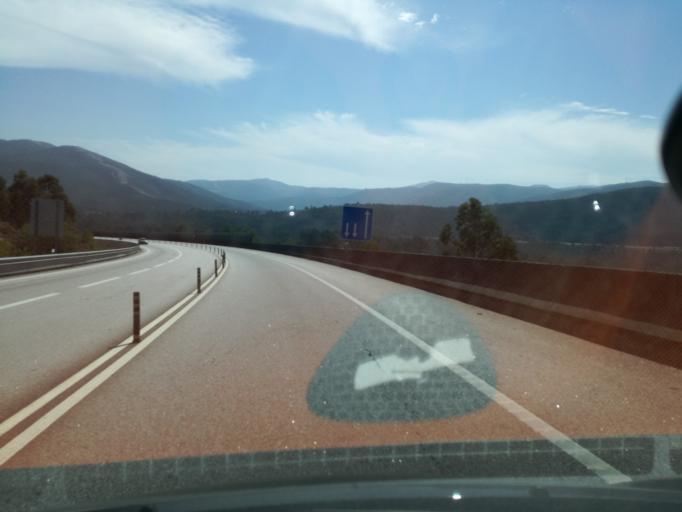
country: PT
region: Viana do Castelo
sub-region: Vila Nova de Cerveira
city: Vila Nova de Cerveira
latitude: 41.8966
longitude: -8.7850
